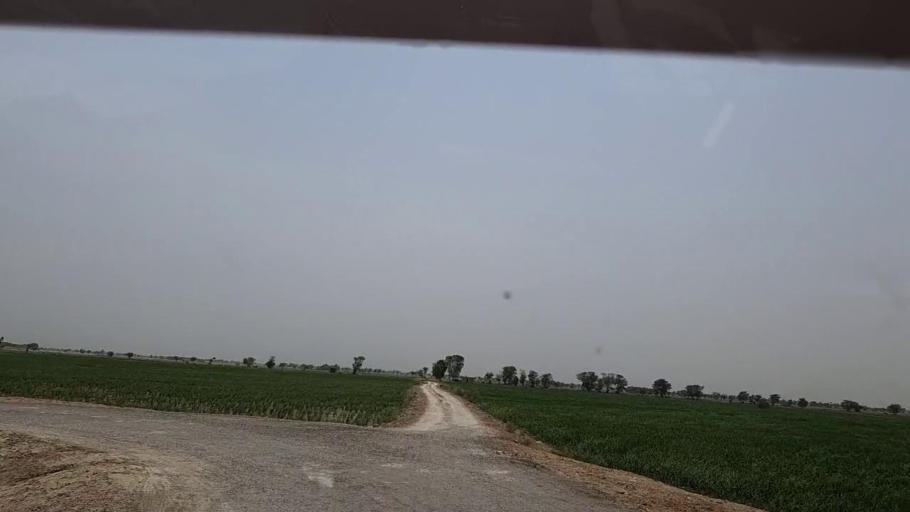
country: PK
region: Sindh
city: Khairpur Nathan Shah
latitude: 27.0163
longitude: 67.6506
